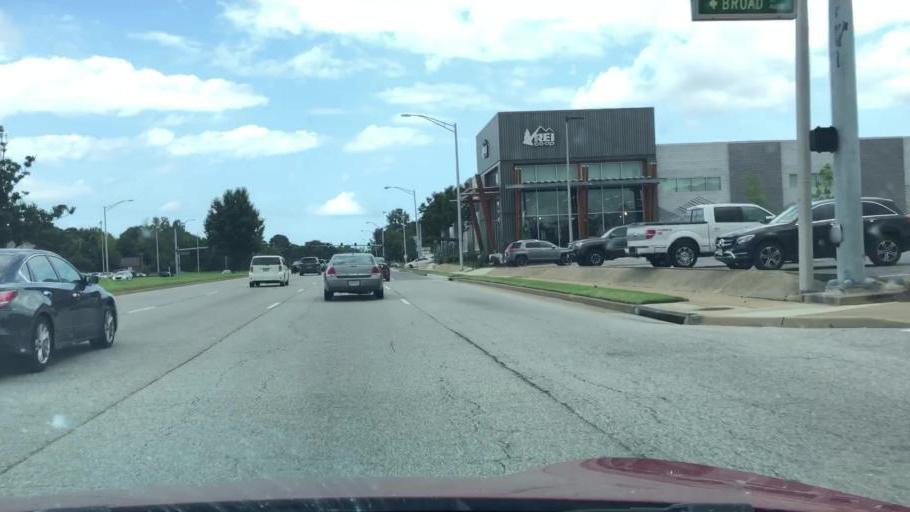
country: US
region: Virginia
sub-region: City of Chesapeake
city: Chesapeake
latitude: 36.8460
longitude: -76.1366
